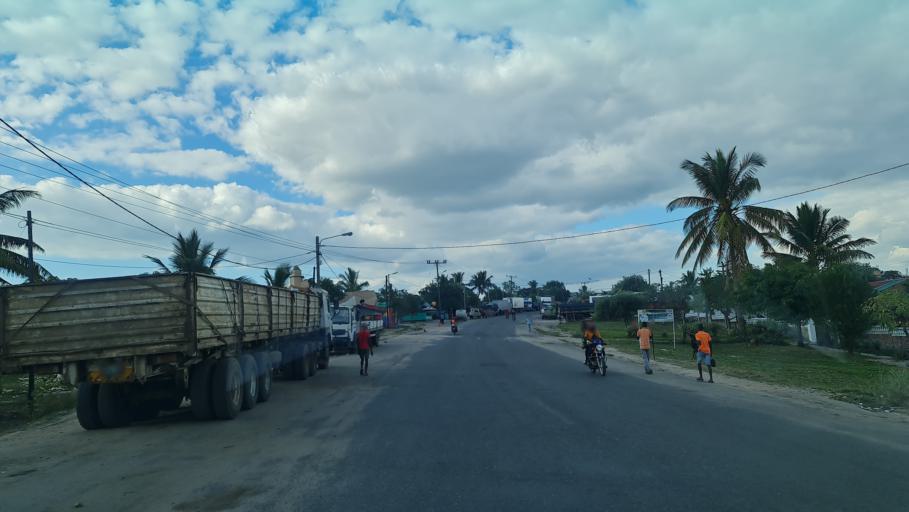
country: MZ
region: Manica
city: Chimoio
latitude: -19.2115
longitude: 33.9249
